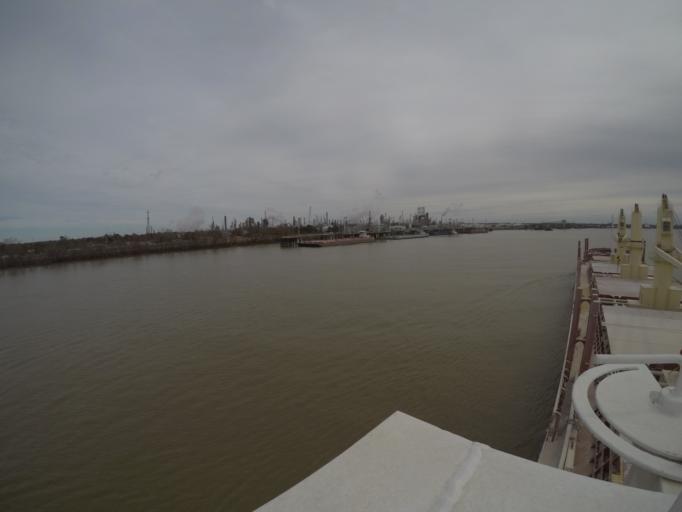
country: US
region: Louisiana
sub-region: Saint Charles Parish
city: Norco
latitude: 29.9935
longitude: -90.4151
